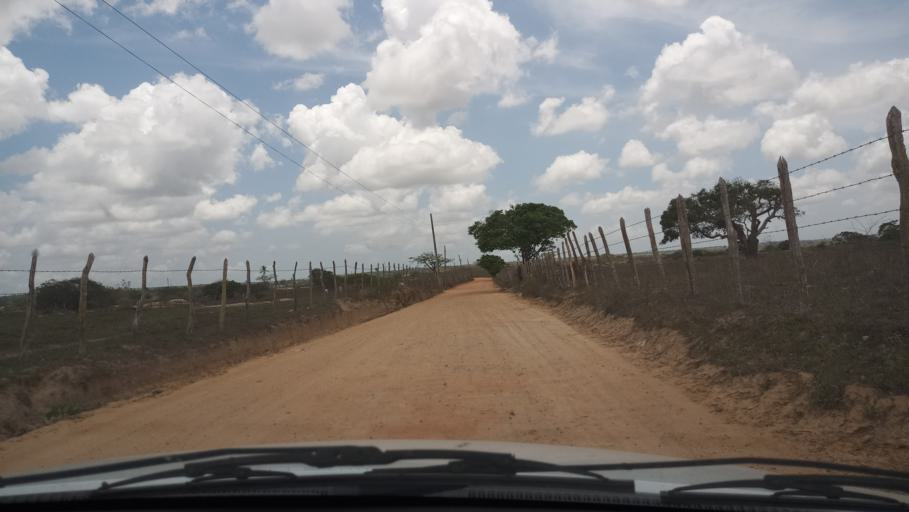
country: BR
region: Rio Grande do Norte
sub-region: Brejinho
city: Brejinho
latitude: -6.2828
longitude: -35.3412
